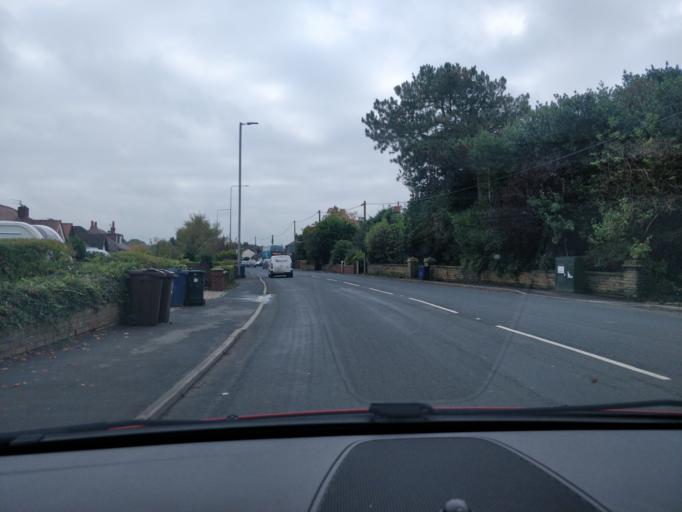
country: GB
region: England
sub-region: Lancashire
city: Banks
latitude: 53.6133
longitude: -2.9401
